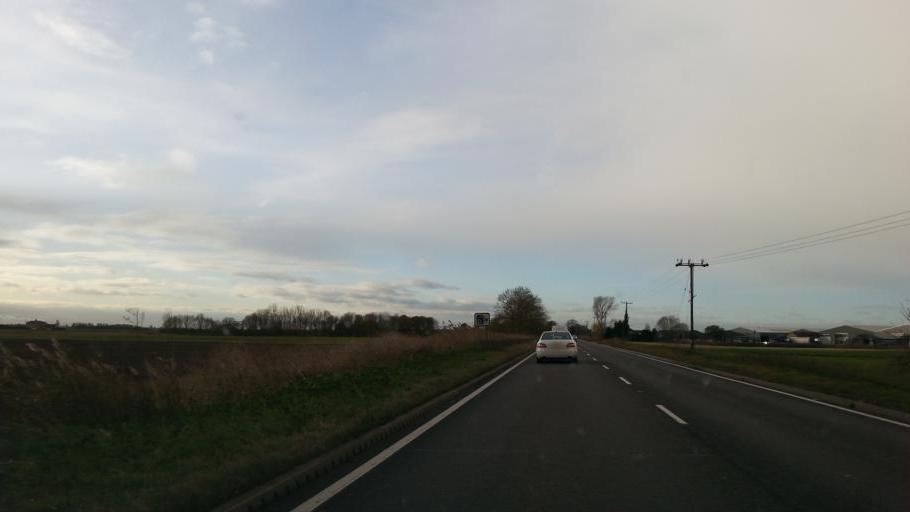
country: GB
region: England
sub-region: Cambridgeshire
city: March
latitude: 52.6132
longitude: 0.0100
